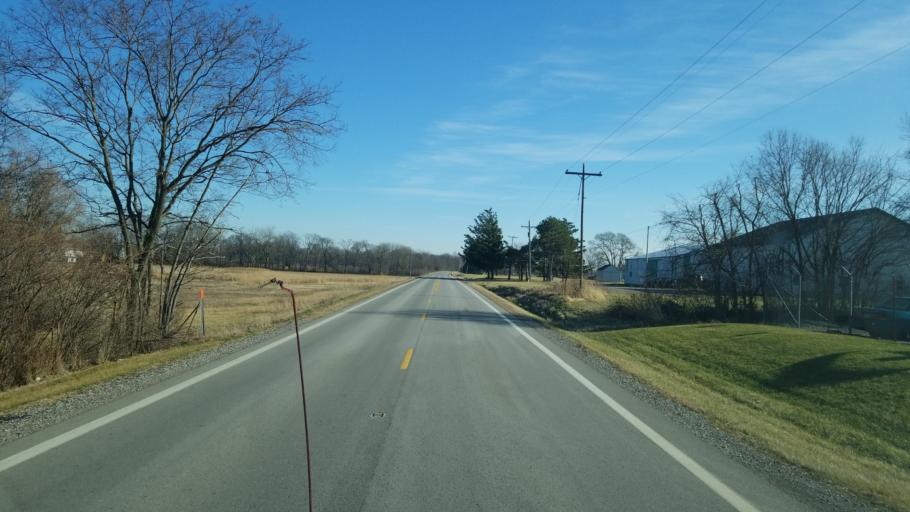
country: US
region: Ohio
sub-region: Henry County
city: Liberty Center
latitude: 41.4147
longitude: -83.9071
